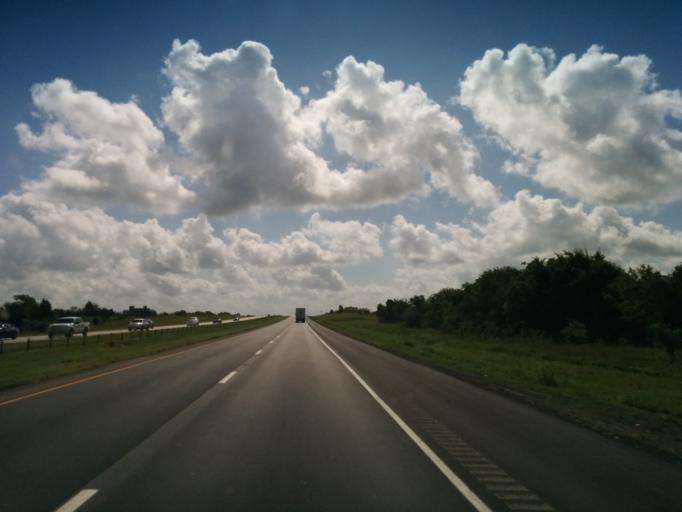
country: US
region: Texas
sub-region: Colorado County
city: Weimar
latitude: 29.6886
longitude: -96.8187
